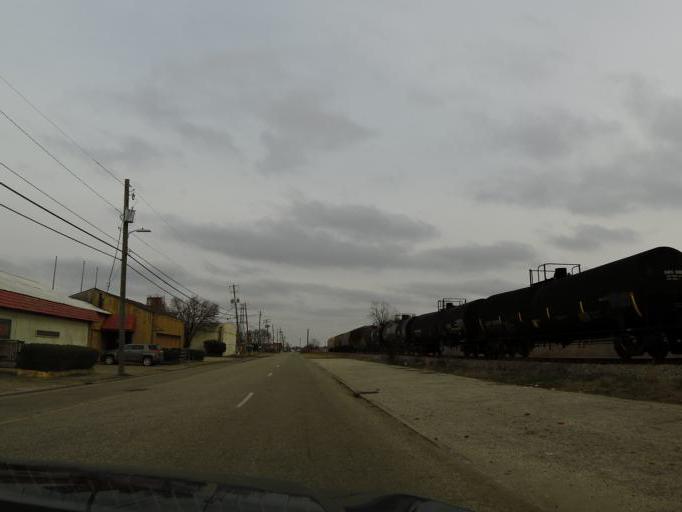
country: US
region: Alabama
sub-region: Montgomery County
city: Montgomery
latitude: 32.3912
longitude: -86.3090
